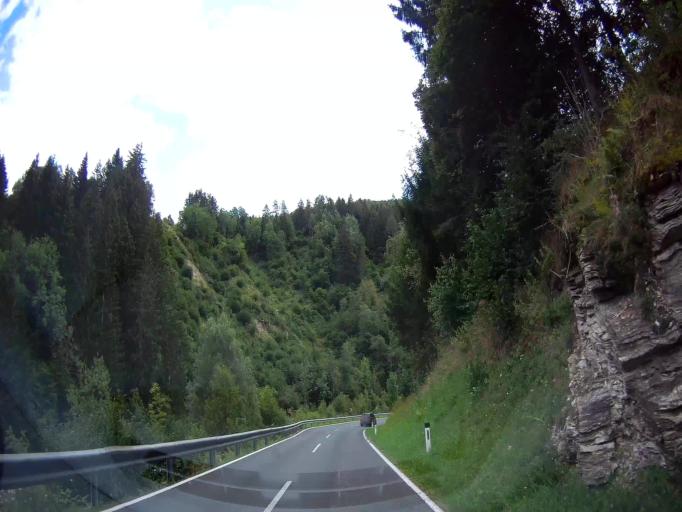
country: AT
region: Carinthia
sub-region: Politischer Bezirk Spittal an der Drau
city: Trebesing
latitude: 46.8880
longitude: 13.5204
